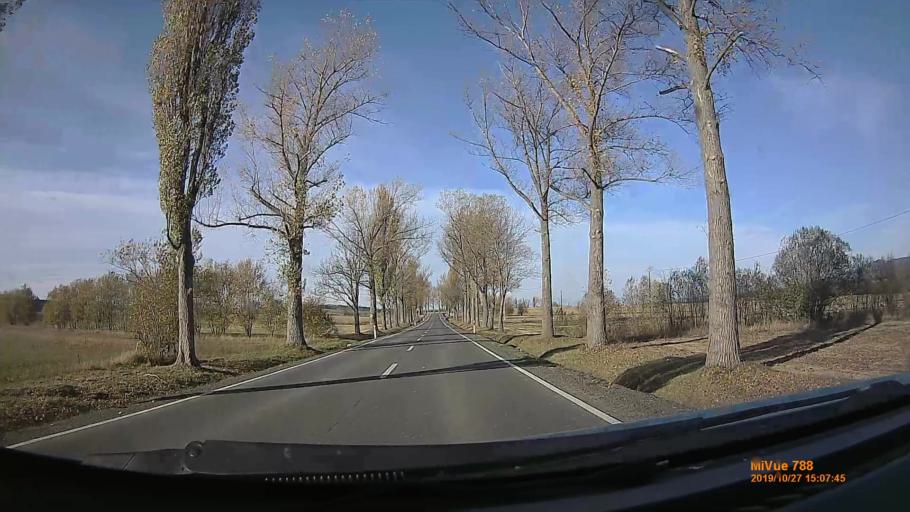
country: PL
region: Lower Silesian Voivodeship
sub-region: Powiat klodzki
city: Miedzylesie
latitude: 50.1611
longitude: 16.6700
